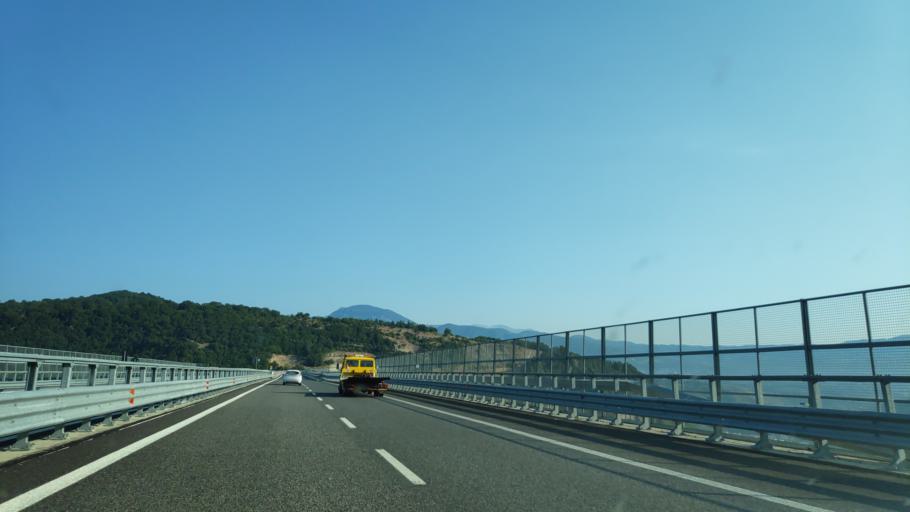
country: IT
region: Calabria
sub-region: Provincia di Cosenza
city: Laino Castello-Nuovo Centro
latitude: 39.9359
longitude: 15.9605
